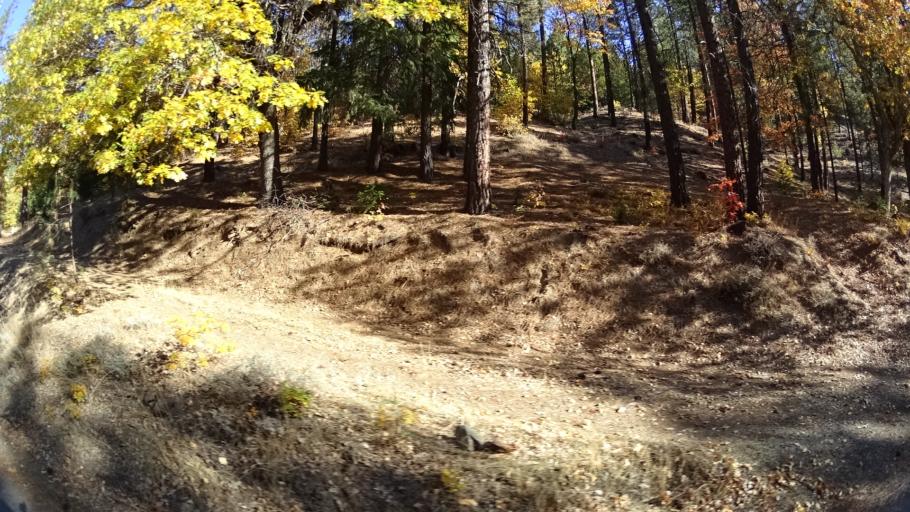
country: US
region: California
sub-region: Siskiyou County
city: Happy Camp
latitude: 41.6430
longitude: -123.0259
